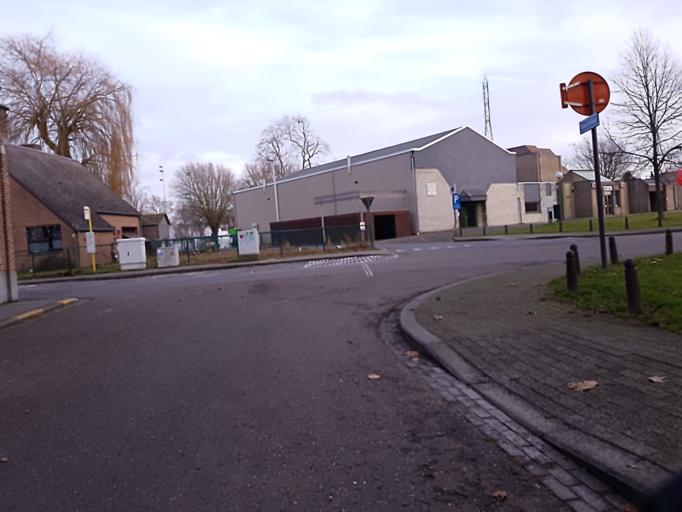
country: BE
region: Flanders
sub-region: Provincie Vlaams-Brabant
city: Rotselaar
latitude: 50.9259
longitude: 4.7051
